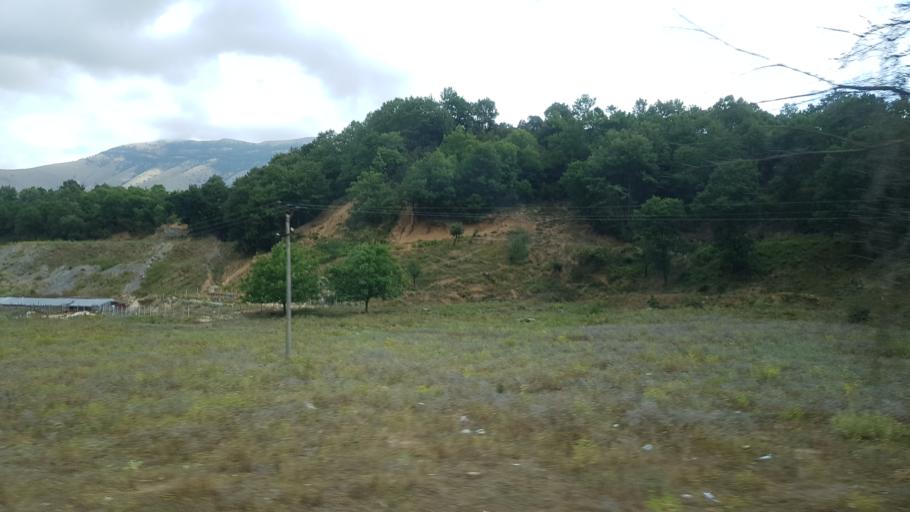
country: AL
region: Vlore
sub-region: Rrethi i Sarandes
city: Dhiver
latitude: 39.9121
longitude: 20.1855
